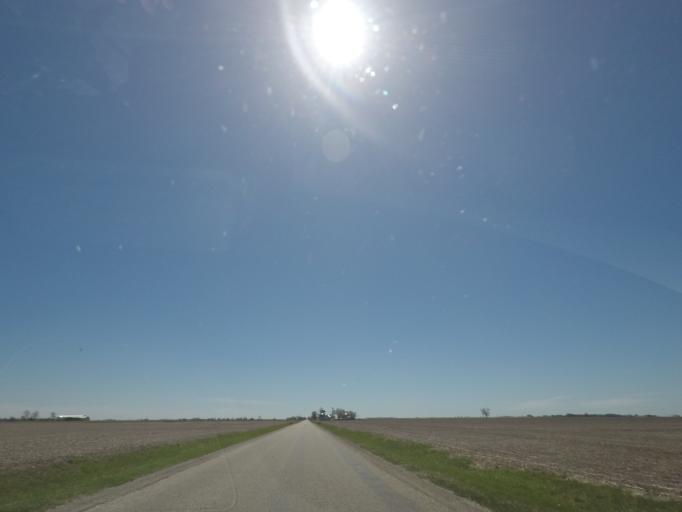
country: US
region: Illinois
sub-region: Logan County
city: Atlanta
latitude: 40.2062
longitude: -89.1943
